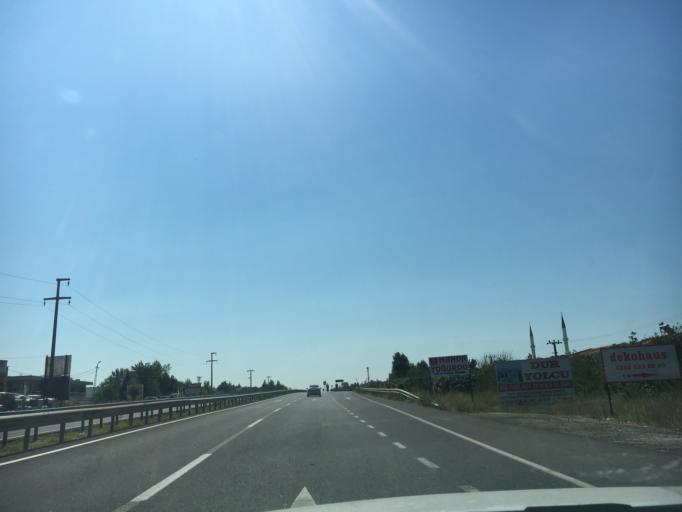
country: TR
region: Tekirdag
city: Marmara Ereglisi
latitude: 40.9758
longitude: 27.8748
